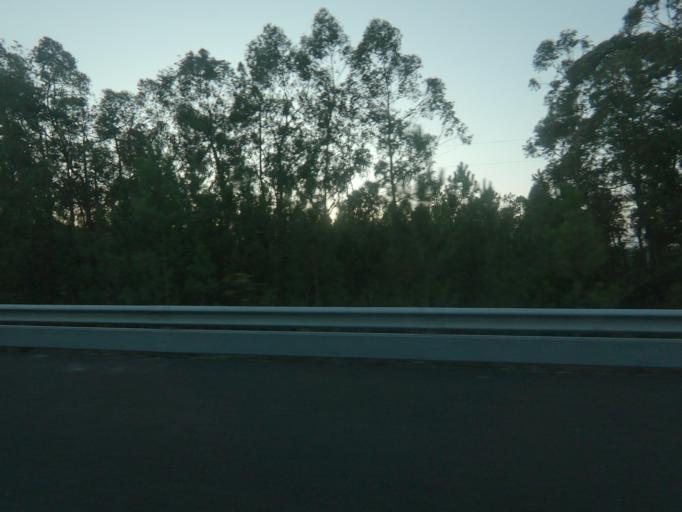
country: PT
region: Leiria
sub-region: Pombal
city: Pombal
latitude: 39.8797
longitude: -8.6985
